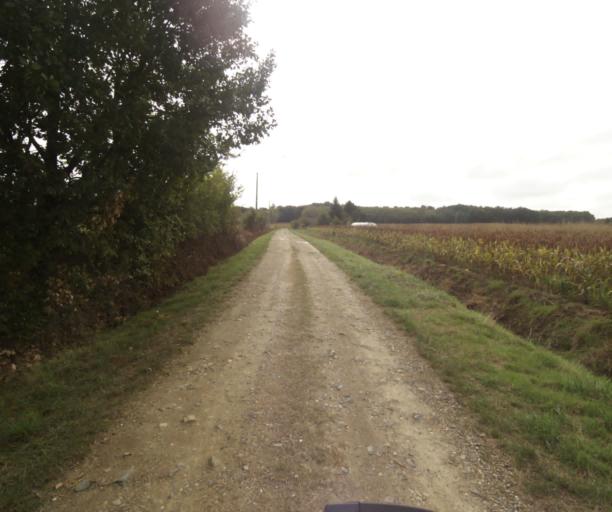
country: FR
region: Midi-Pyrenees
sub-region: Departement du Tarn-et-Garonne
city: Campsas
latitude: 43.9195
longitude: 1.2967
